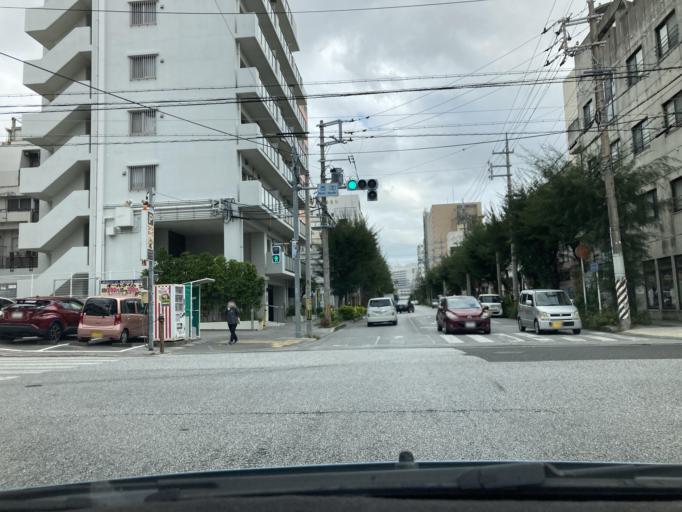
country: JP
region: Okinawa
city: Naha-shi
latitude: 26.2149
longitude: 127.6711
